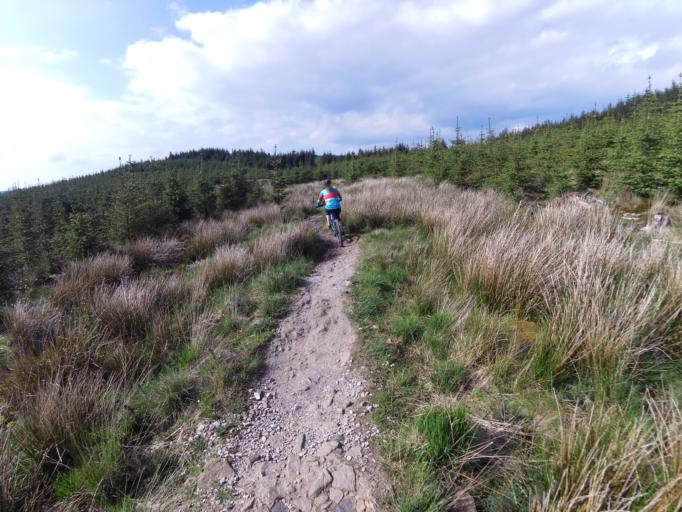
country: GB
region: England
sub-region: North Yorkshire
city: Settle
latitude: 54.0197
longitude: -2.3713
